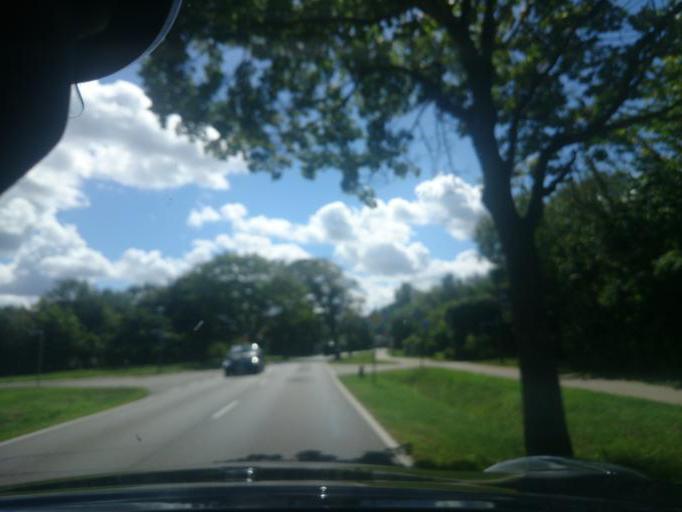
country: DE
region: Mecklenburg-Vorpommern
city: Elmenhorst
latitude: 54.1450
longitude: 12.0272
